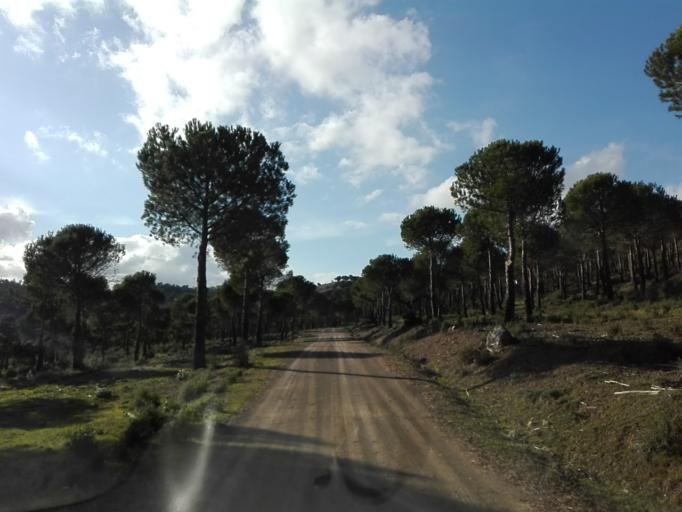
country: ES
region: Extremadura
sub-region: Provincia de Badajoz
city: Reina
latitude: 38.1767
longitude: -5.9692
